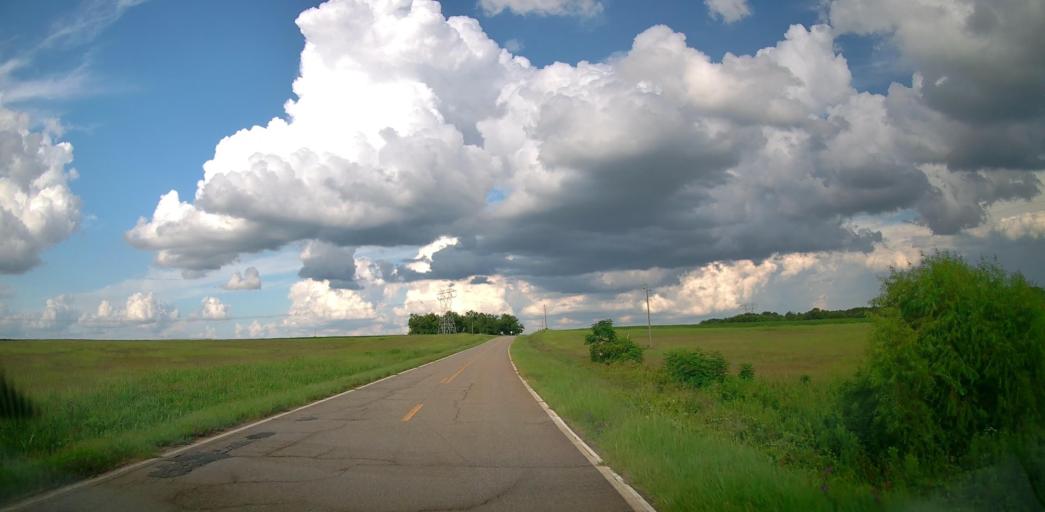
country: US
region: Georgia
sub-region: Bleckley County
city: Cochran
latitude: 32.4060
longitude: -83.4149
